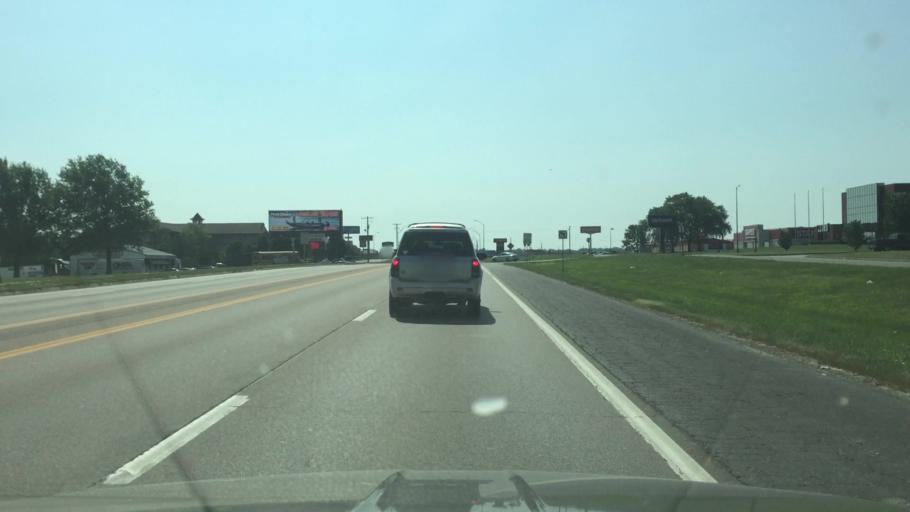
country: US
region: Missouri
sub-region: Pettis County
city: Sedalia
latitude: 38.7121
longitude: -93.2756
